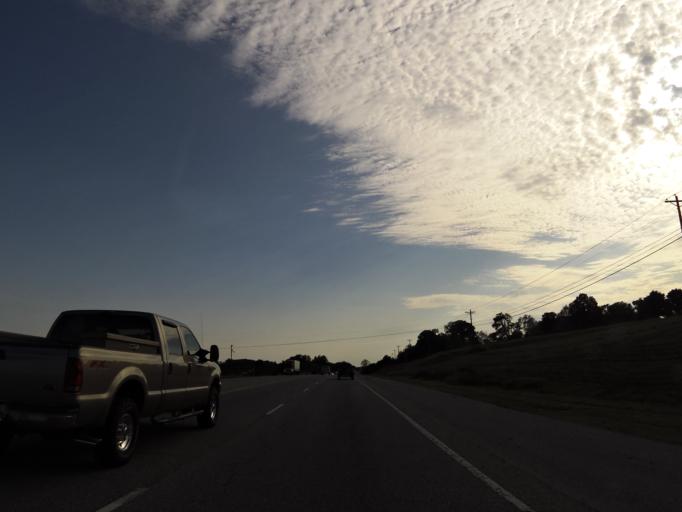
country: US
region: Tennessee
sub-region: Blount County
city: Maryville
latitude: 35.6923
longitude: -84.0513
